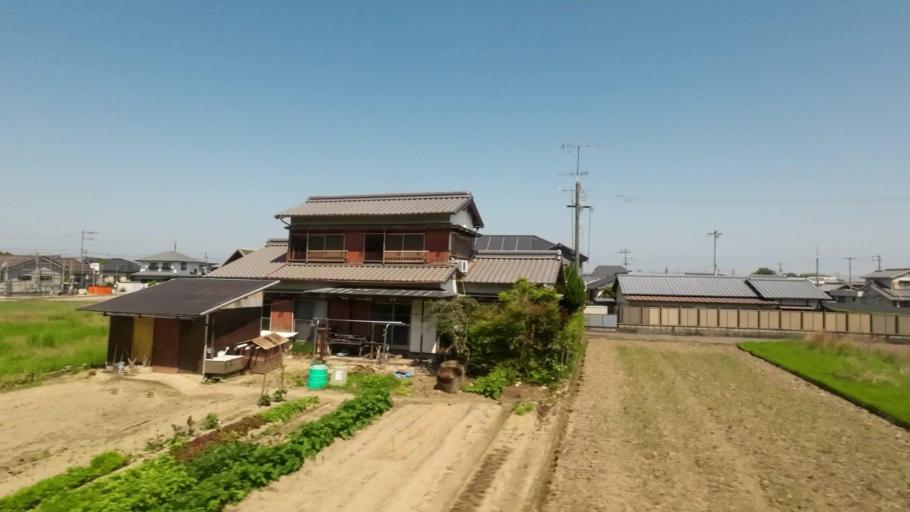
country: JP
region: Ehime
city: Niihama
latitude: 33.9639
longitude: 133.3140
